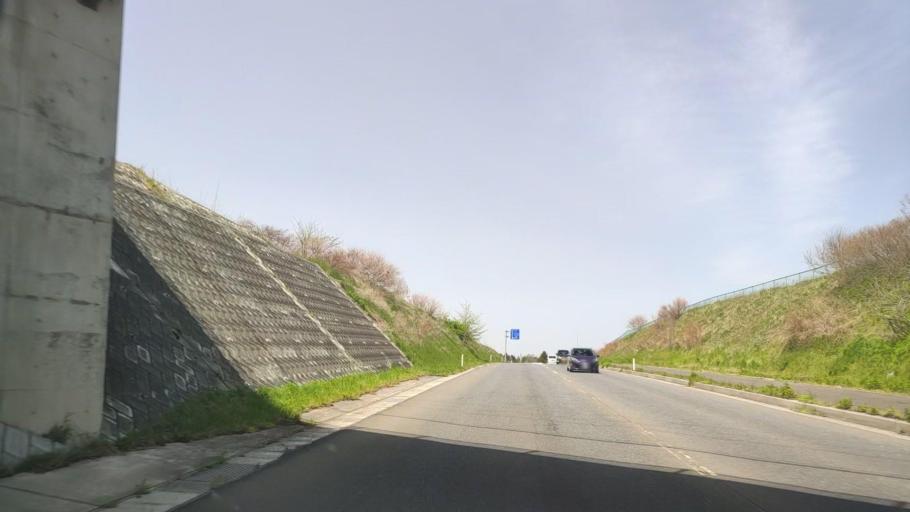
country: JP
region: Aomori
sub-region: Hachinohe Shi
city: Uchimaru
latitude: 40.5267
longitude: 141.4103
